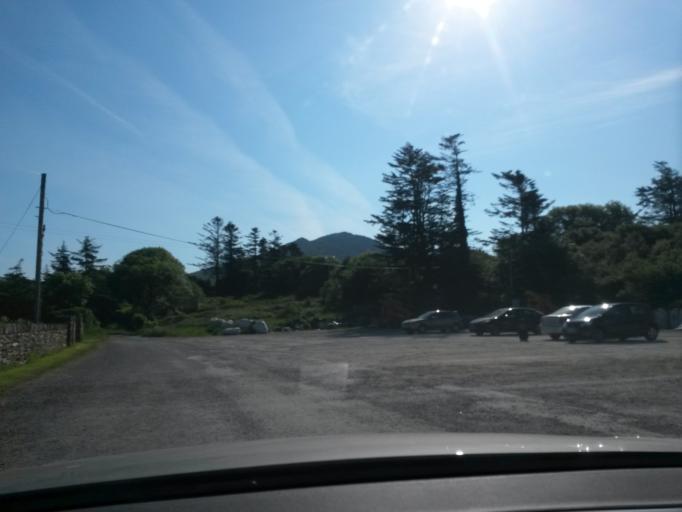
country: IE
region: Munster
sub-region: Ciarrai
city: Kenmare
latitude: 51.7805
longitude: -9.8054
